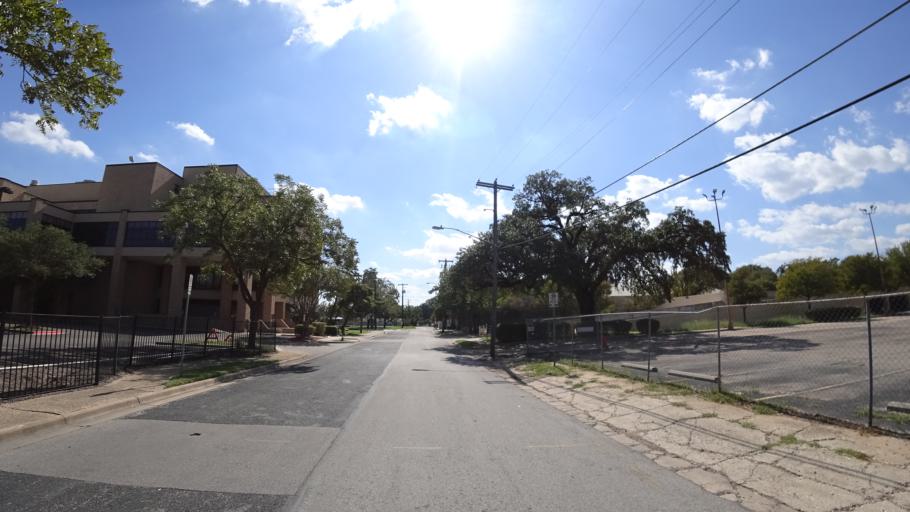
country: US
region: Texas
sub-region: Travis County
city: Austin
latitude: 30.3035
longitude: -97.7470
